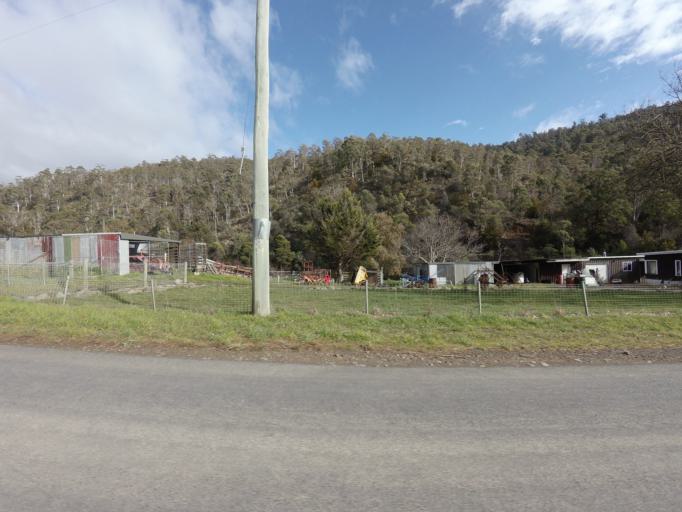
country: AU
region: Tasmania
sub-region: Derwent Valley
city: New Norfolk
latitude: -42.7843
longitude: 146.9469
